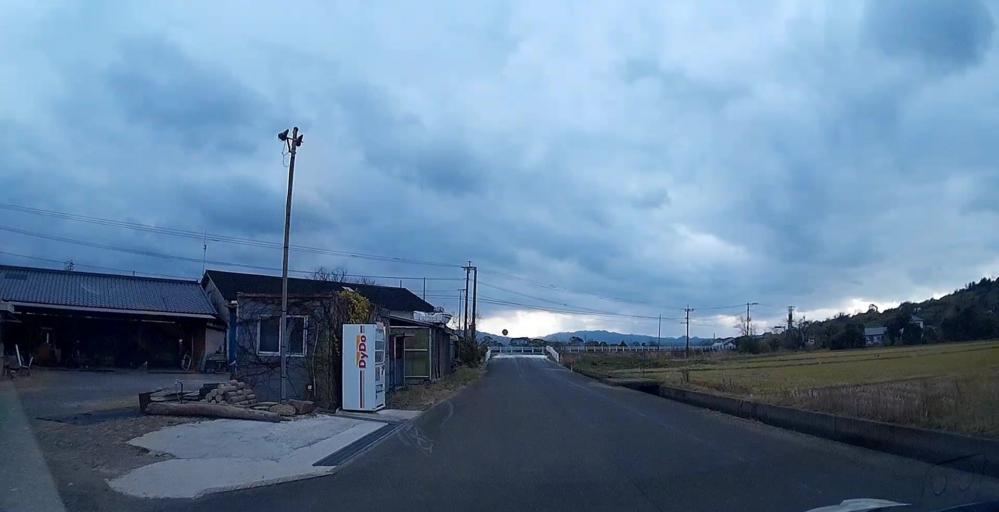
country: JP
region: Kagoshima
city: Izumi
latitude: 32.0964
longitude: 130.2756
